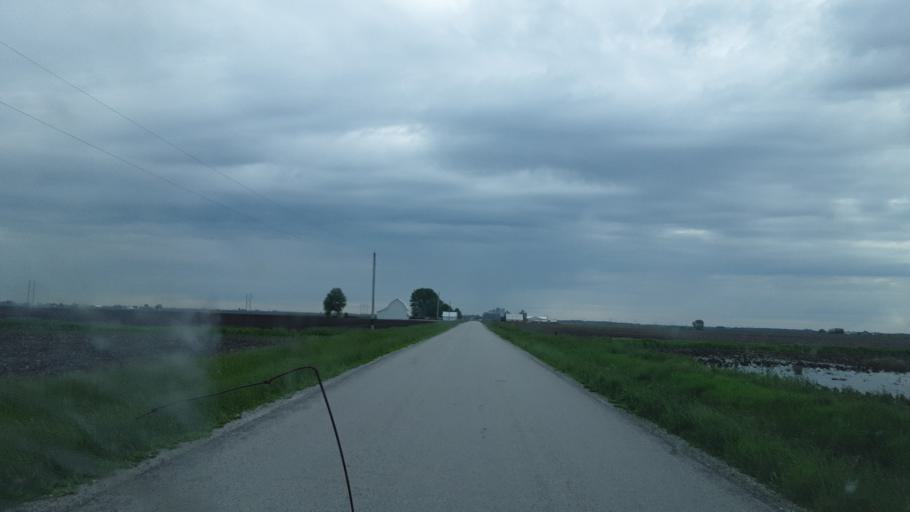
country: US
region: Illinois
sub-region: McDonough County
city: Macomb
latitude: 40.3815
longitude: -90.5361
